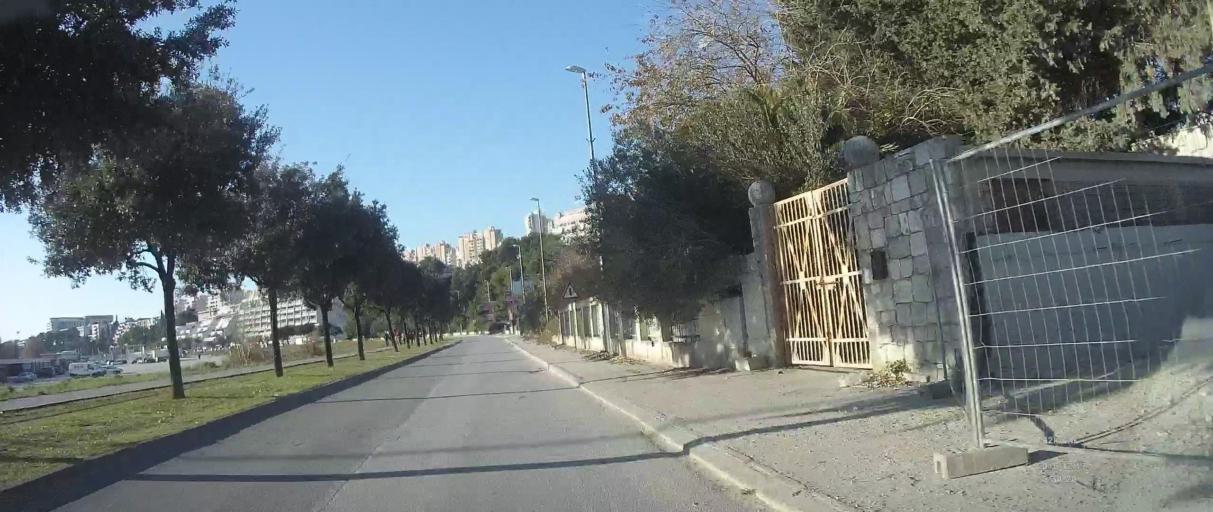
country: HR
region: Splitsko-Dalmatinska
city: Vranjic
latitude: 43.5026
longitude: 16.4809
